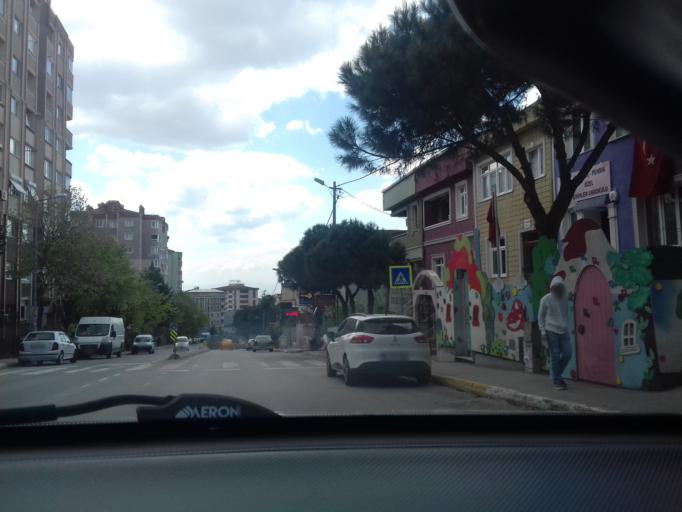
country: TR
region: Istanbul
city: Pendik
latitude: 40.9125
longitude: 29.2826
